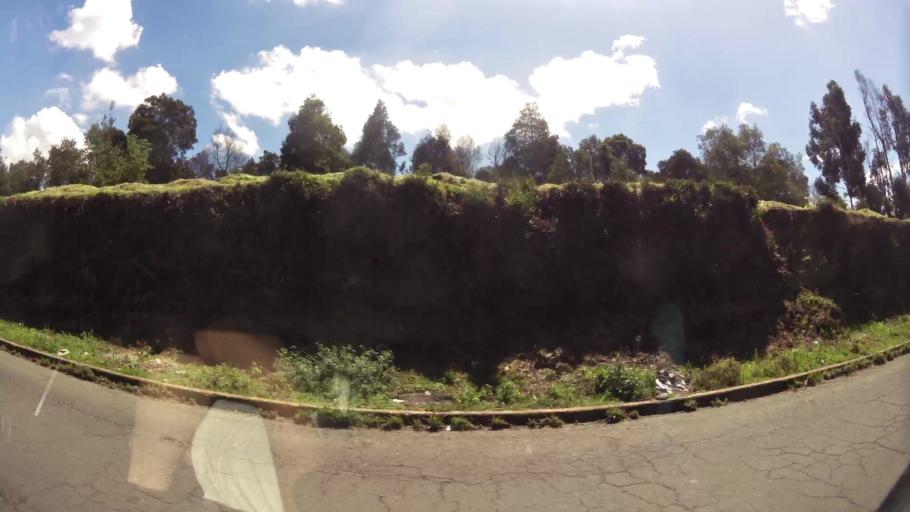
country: EC
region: Pichincha
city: Quito
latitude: -0.2897
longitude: -78.5483
